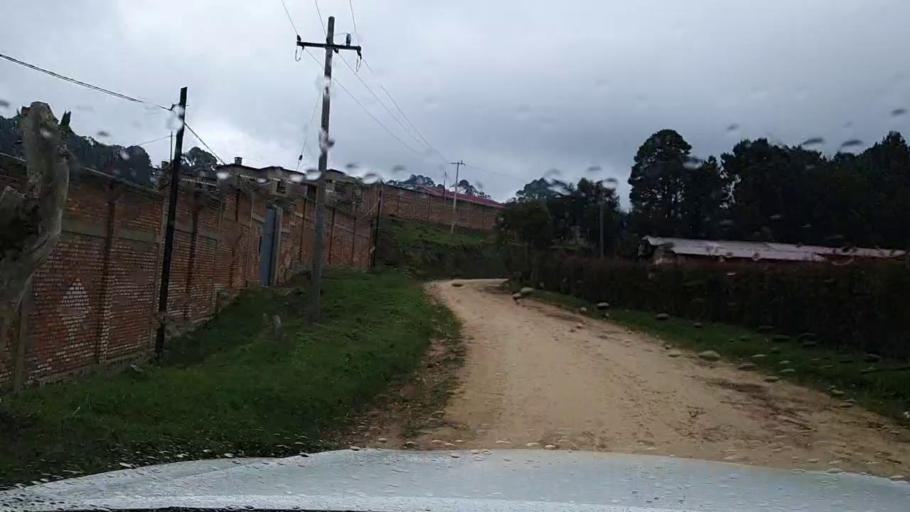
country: RW
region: Southern Province
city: Nzega
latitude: -2.3688
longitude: 29.3813
